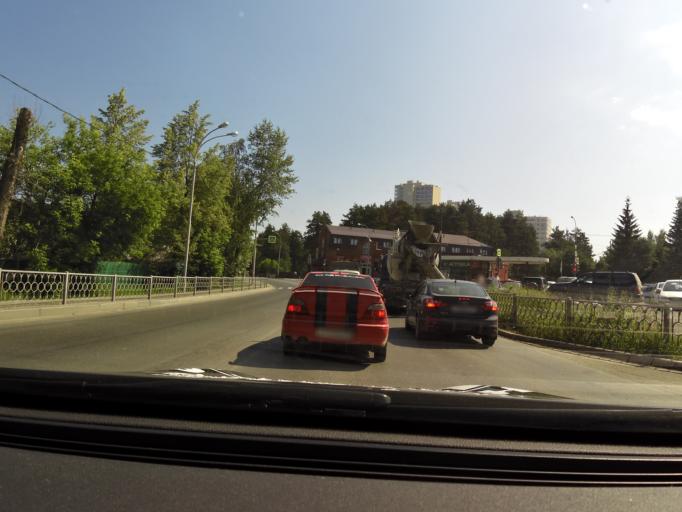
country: RU
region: Sverdlovsk
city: Shirokaya Rechka
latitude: 56.8101
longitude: 60.5070
